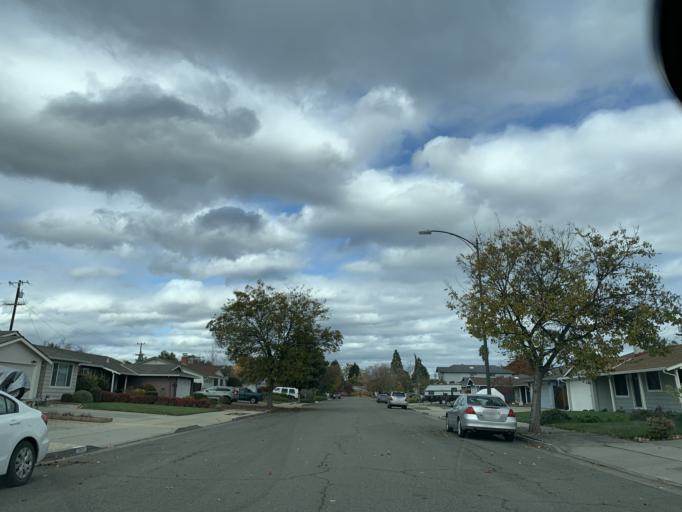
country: US
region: California
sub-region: Santa Clara County
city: Campbell
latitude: 37.2725
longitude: -121.9774
